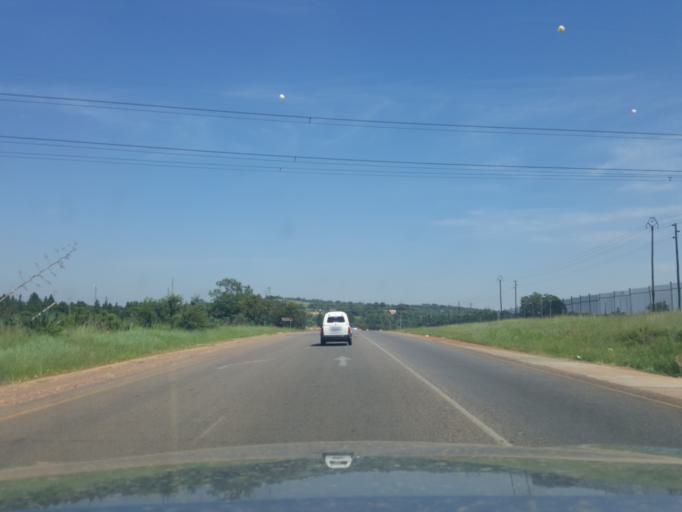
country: ZA
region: Gauteng
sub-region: City of Tshwane Metropolitan Municipality
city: Pretoria
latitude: -25.6763
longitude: 28.3449
